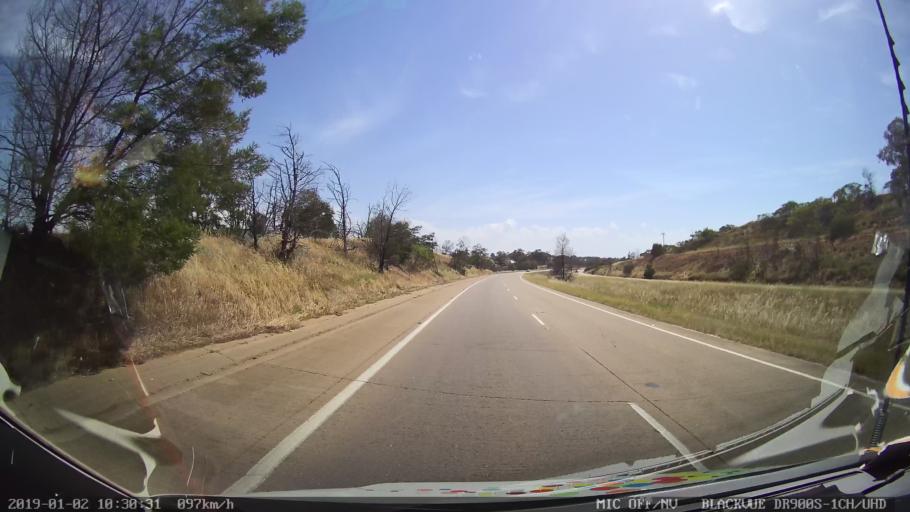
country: AU
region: New South Wales
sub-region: Gundagai
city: Gundagai
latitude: -34.8865
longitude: 148.2200
